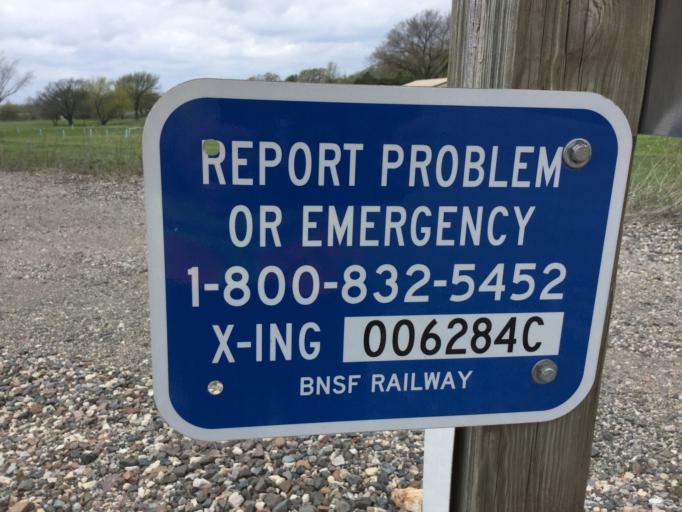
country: US
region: Kansas
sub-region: Osage County
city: Osage City
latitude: 38.4124
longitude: -95.8632
